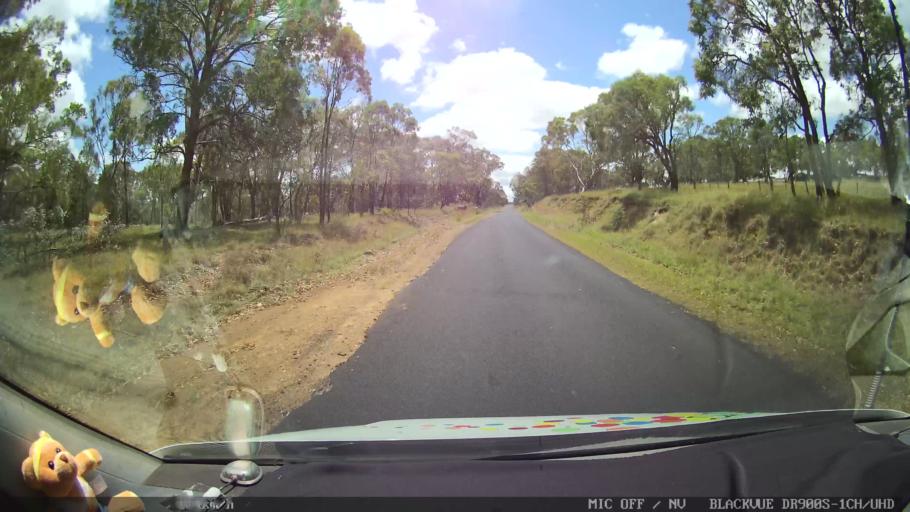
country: AU
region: New South Wales
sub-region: Glen Innes Severn
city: Glen Innes
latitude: -29.4324
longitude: 151.6861
